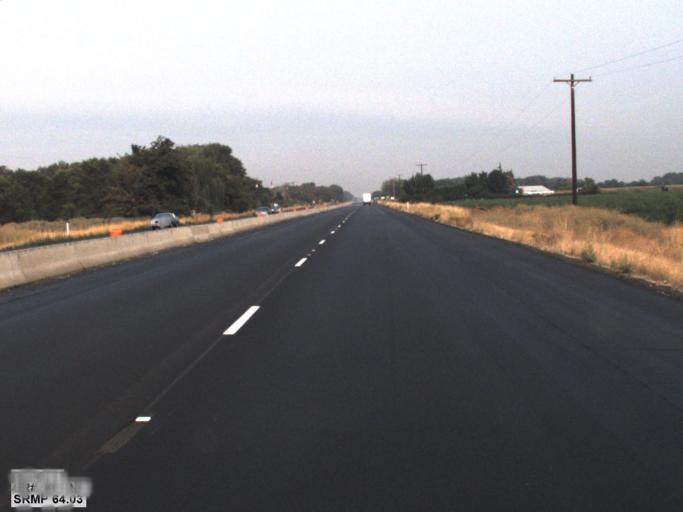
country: US
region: Washington
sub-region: Yakima County
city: Toppenish
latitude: 46.3929
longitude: -120.3631
